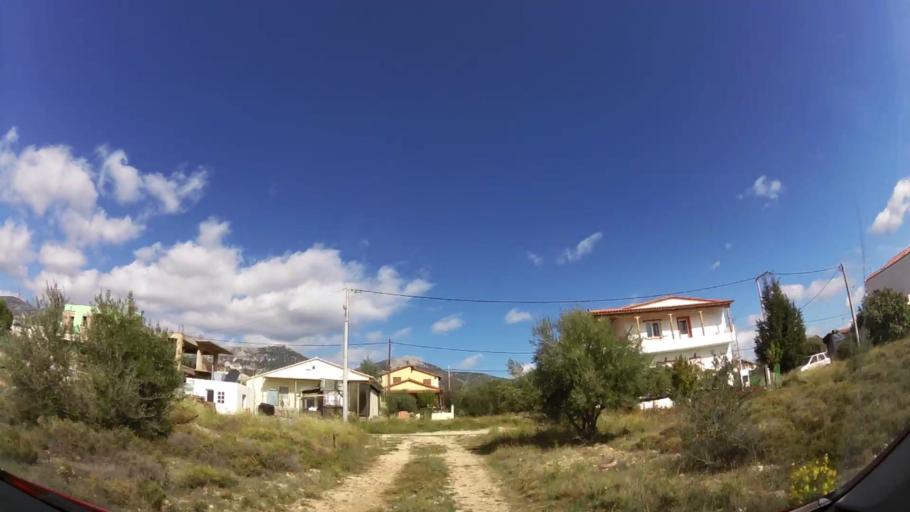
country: GR
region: Attica
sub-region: Nomarchia Anatolikis Attikis
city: Thrakomakedones
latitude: 38.1170
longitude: 23.7504
